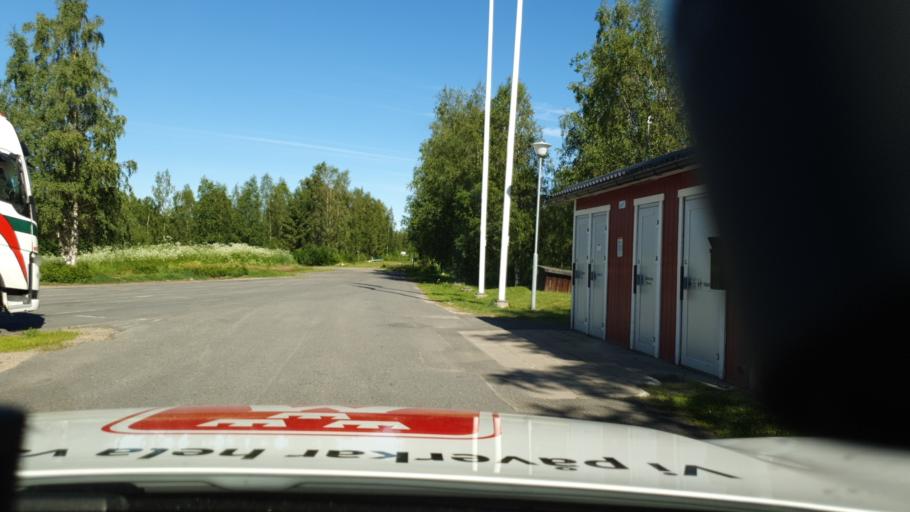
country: SE
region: Norrbotten
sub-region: Haparanda Kommun
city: Haparanda
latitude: 65.8104
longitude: 23.9326
